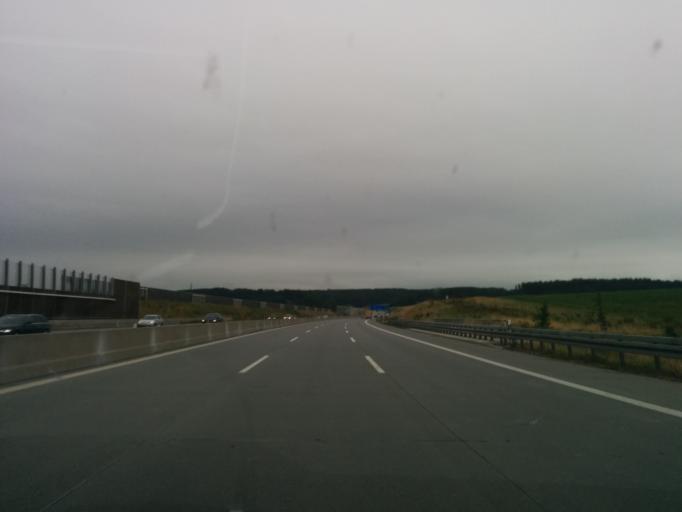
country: DE
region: Bavaria
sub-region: Swabia
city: Adelzhausen
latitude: 48.3601
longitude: 11.1273
